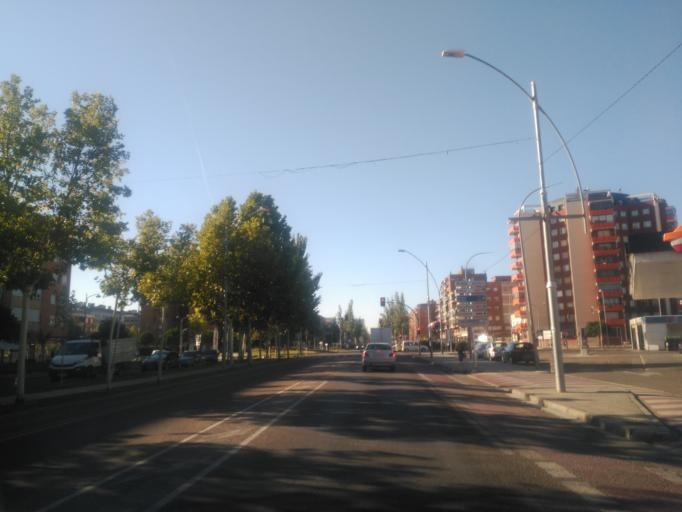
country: ES
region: Castille and Leon
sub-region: Provincia de Burgos
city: Aranda de Duero
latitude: 41.6630
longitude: -3.6916
